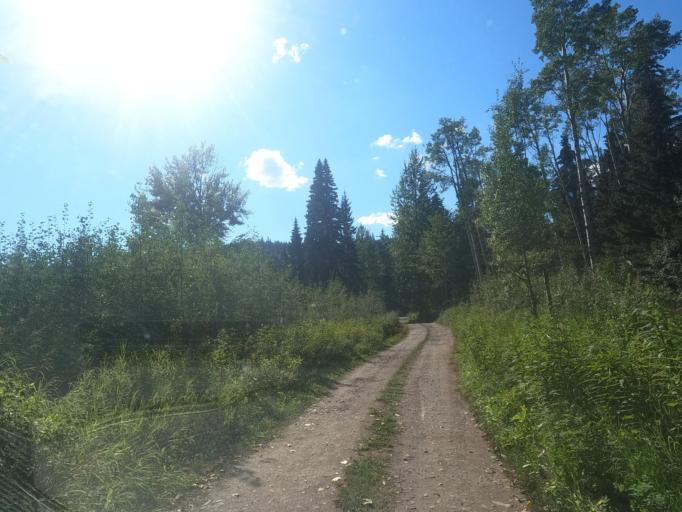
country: CA
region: British Columbia
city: Houston
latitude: 54.2863
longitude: -126.8552
